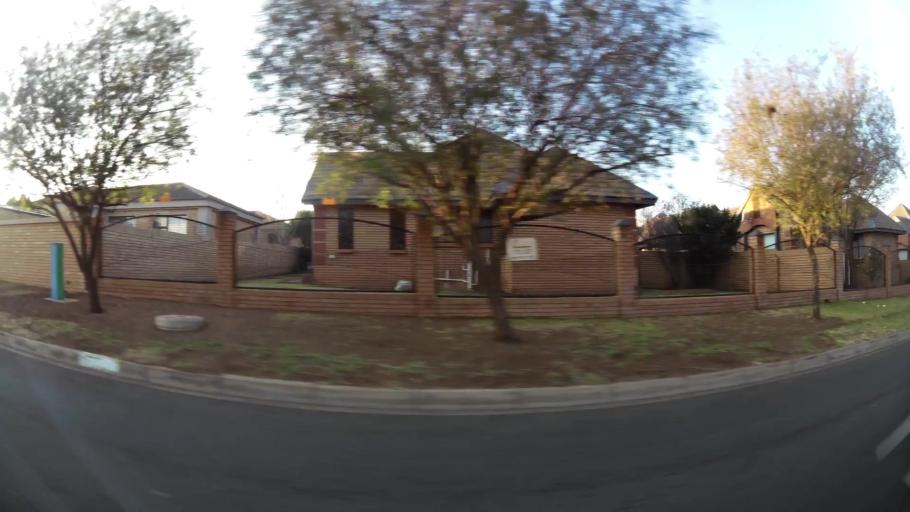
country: ZA
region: Orange Free State
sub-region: Mangaung Metropolitan Municipality
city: Bloemfontein
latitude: -29.0943
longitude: 26.1666
